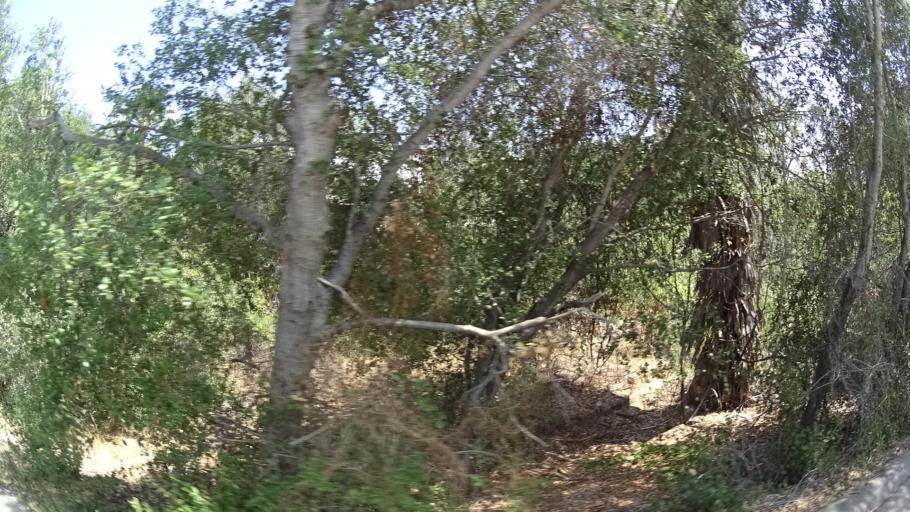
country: US
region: California
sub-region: San Diego County
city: Bonsall
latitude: 33.3165
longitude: -117.2072
